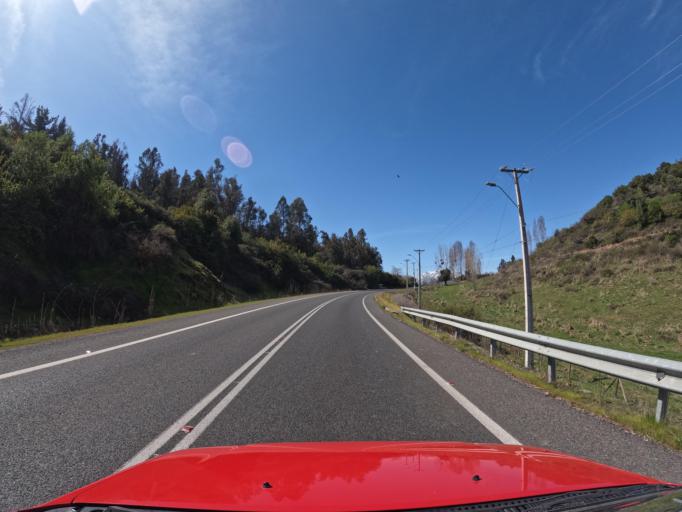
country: CL
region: Maule
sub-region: Provincia de Curico
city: Teno
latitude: -34.9780
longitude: -70.9676
